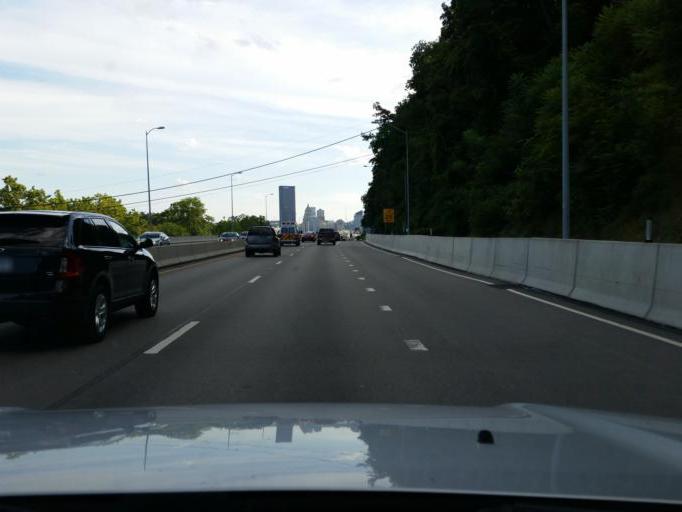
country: US
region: Pennsylvania
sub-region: Allegheny County
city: Millvale
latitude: 40.4686
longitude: -79.9768
